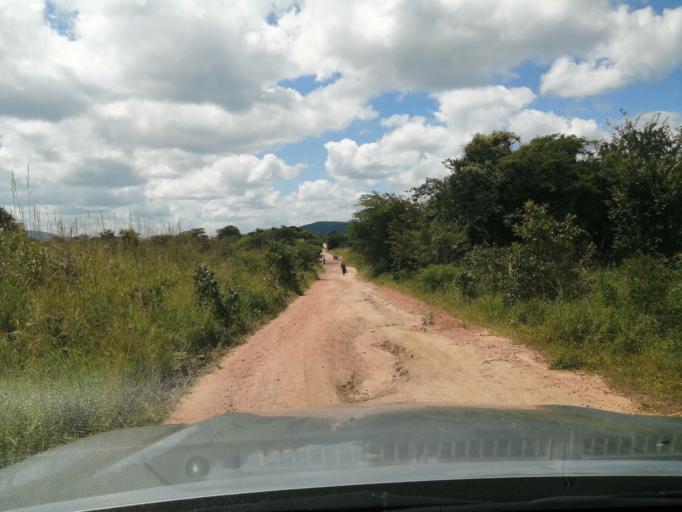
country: ZM
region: Lusaka
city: Lusaka
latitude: -15.1311
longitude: 27.8966
